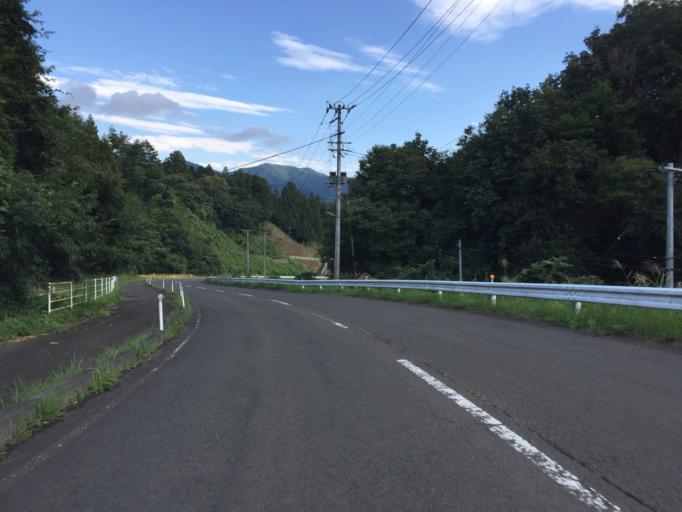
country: JP
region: Fukushima
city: Fukushima-shi
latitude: 37.6544
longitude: 140.5675
